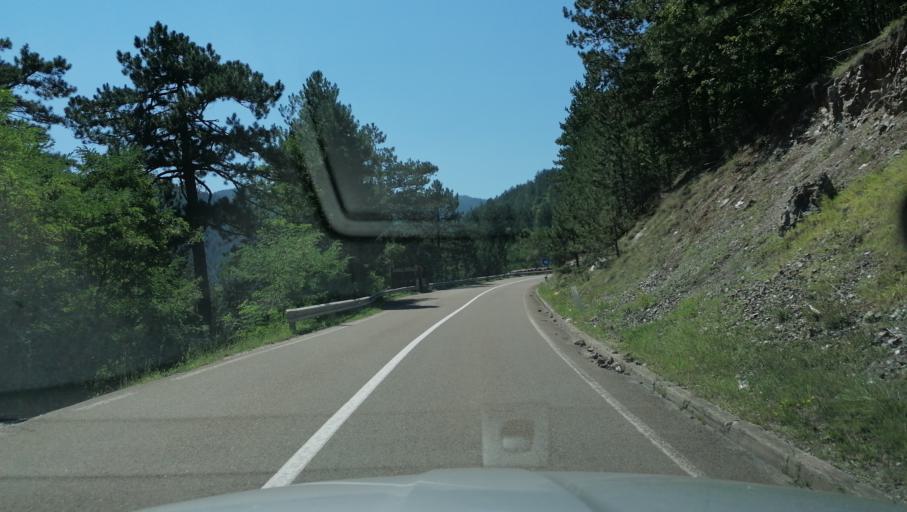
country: RS
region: Central Serbia
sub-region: Raski Okrug
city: Raska
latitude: 43.4611
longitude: 20.5991
